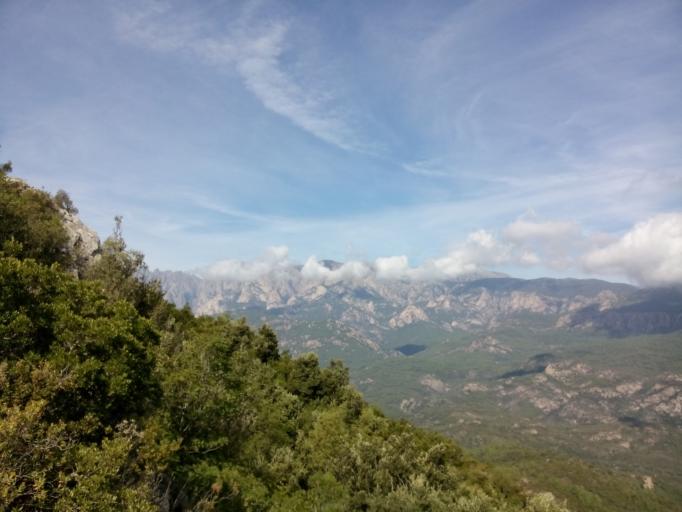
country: FR
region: Corsica
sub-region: Departement de la Corse-du-Sud
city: Sari-Solenzara
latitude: 41.8274
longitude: 9.3625
